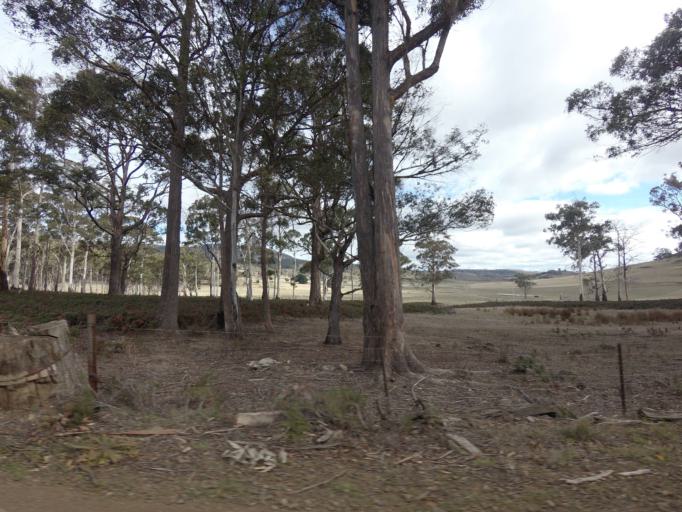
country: AU
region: Tasmania
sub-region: Brighton
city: Bridgewater
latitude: -42.4840
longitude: 147.3016
